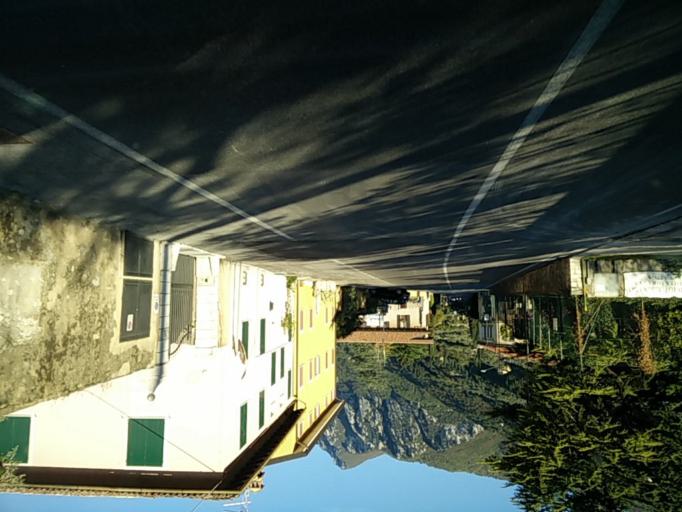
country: IT
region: Lombardy
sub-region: Provincia di Brescia
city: Gargnano
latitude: 45.6781
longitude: 10.6536
